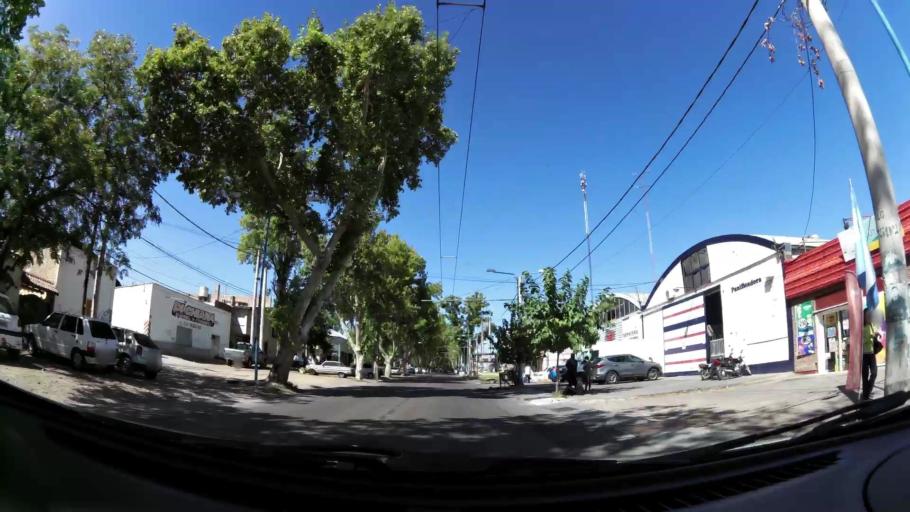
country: AR
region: Mendoza
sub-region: Departamento de Godoy Cruz
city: Godoy Cruz
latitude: -32.9403
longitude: -68.8415
